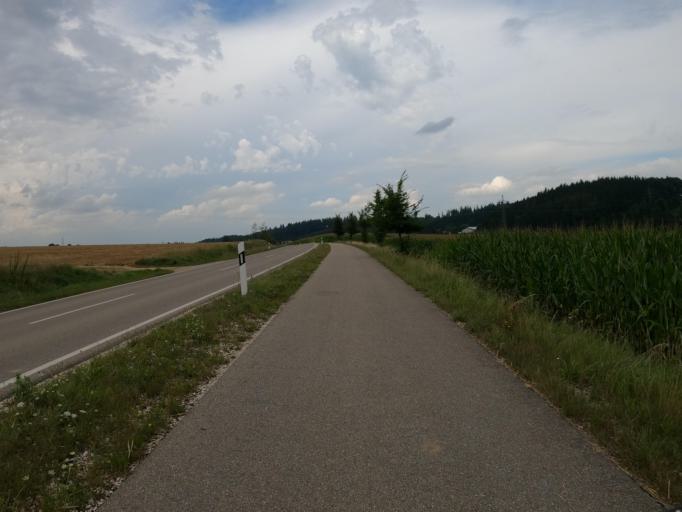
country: DE
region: Bavaria
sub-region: Swabia
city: Pfaffenhofen an der Roth
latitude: 48.3677
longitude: 10.2039
